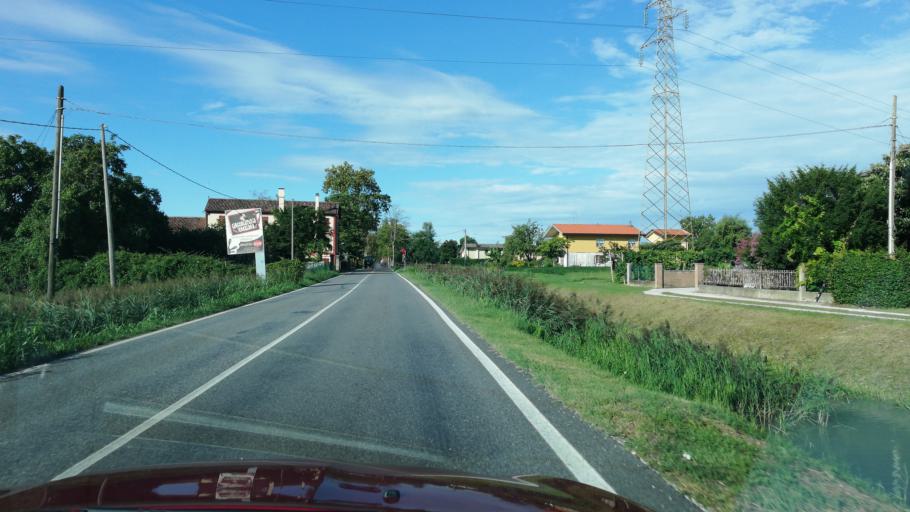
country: IT
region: Veneto
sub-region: Provincia di Venezia
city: Passarella
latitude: 45.5860
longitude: 12.5766
